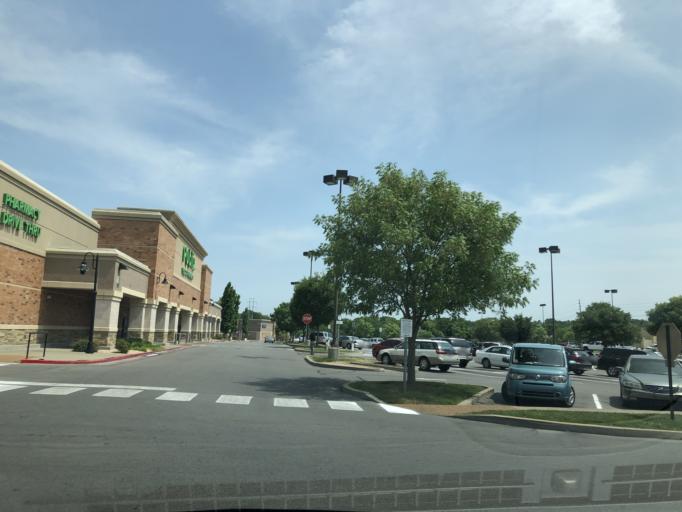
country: US
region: Tennessee
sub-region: Rutherford County
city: La Vergne
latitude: 36.0536
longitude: -86.6157
